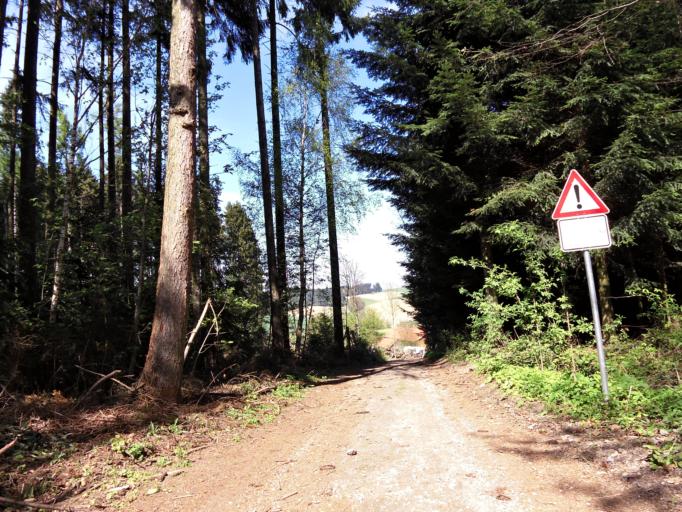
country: DE
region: Bavaria
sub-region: Upper Bavaria
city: Fraunberg
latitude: 48.3411
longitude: 12.0082
